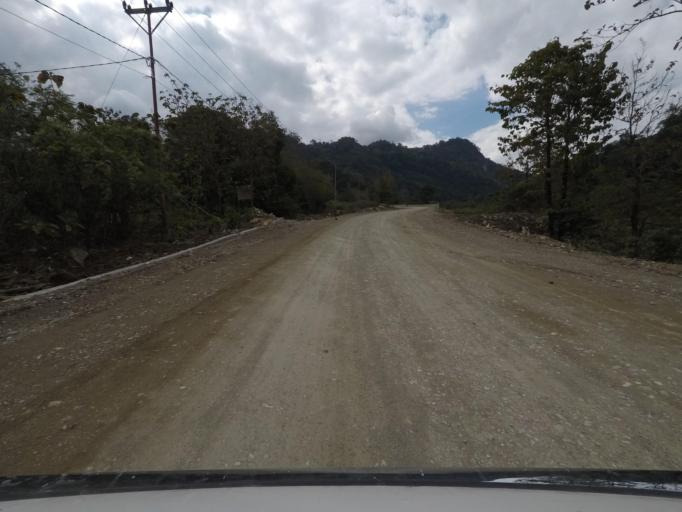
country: TL
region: Viqueque
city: Viqueque
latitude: -8.7768
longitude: 126.3777
